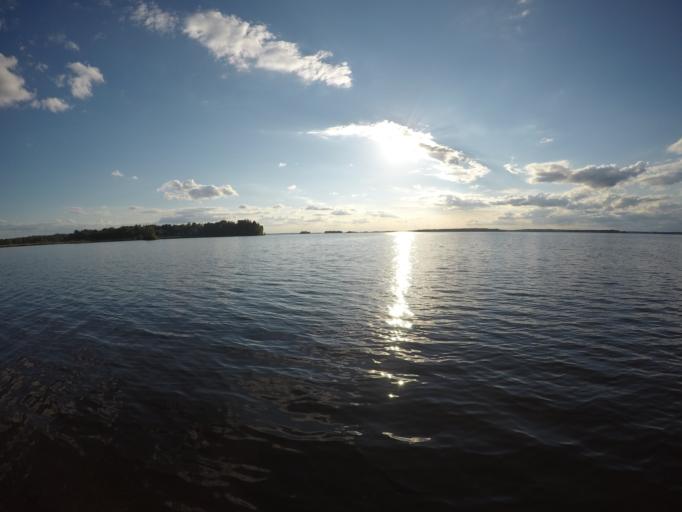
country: SE
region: Soedermanland
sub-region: Eskilstuna Kommun
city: Kvicksund
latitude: 59.4516
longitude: 16.2910
